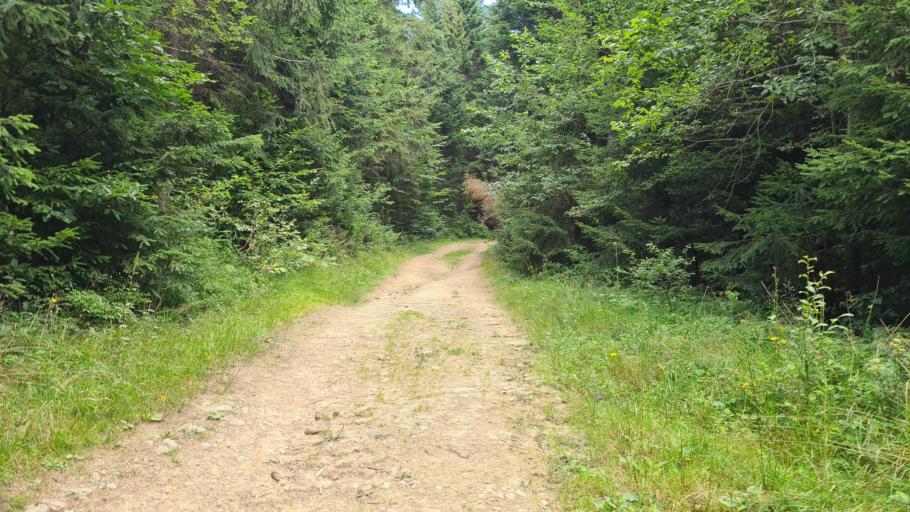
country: PL
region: Lesser Poland Voivodeship
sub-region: Powiat nowosadecki
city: Rytro
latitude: 49.4152
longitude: 20.6223
